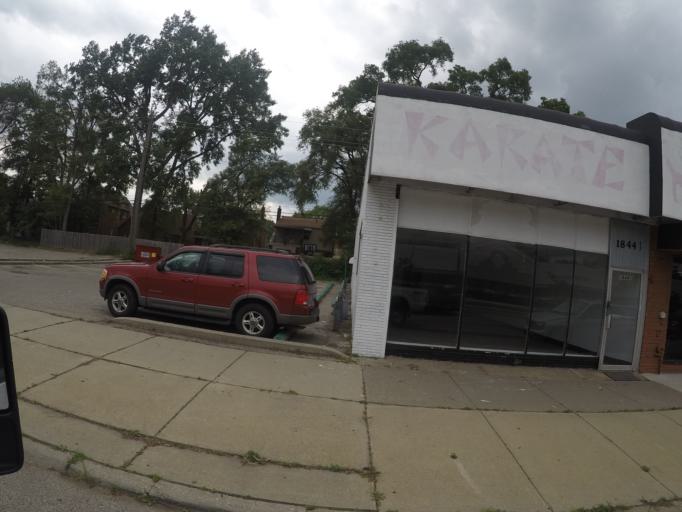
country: US
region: Michigan
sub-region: Oakland County
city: Ferndale
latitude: 42.4269
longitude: -83.1415
